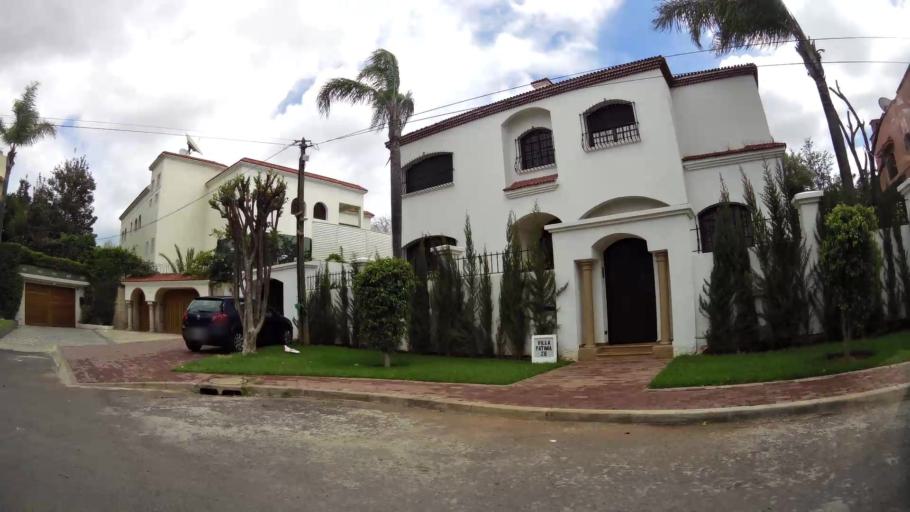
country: MA
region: Grand Casablanca
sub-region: Casablanca
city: Casablanca
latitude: 33.5613
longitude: -7.6226
